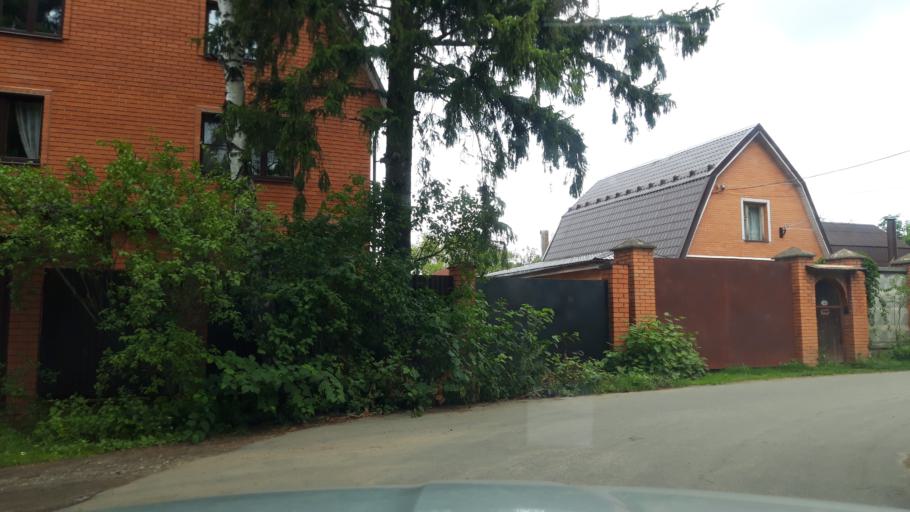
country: RU
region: Moskovskaya
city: Povarovo
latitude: 56.0624
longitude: 37.0688
